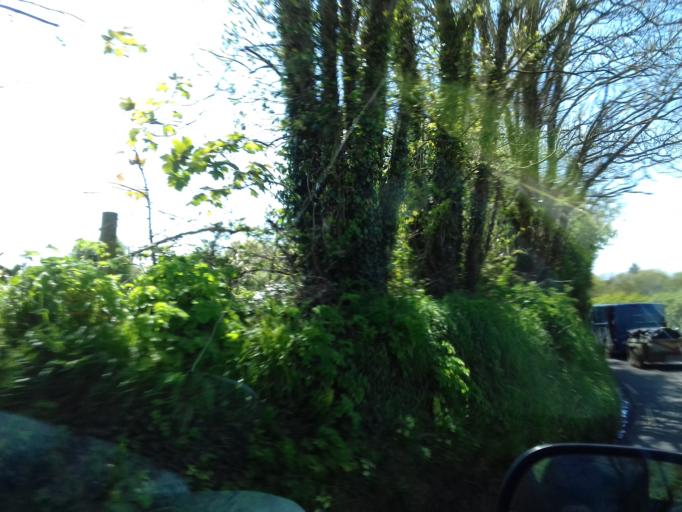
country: IE
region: Munster
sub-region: Waterford
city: Dunmore East
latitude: 52.2138
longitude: -6.8595
